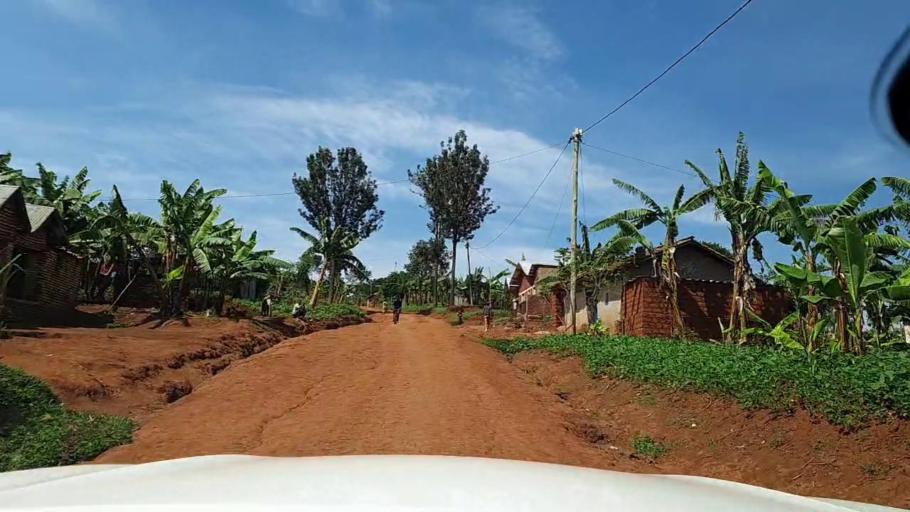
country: RW
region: Southern Province
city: Butare
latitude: -2.7001
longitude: 29.8512
